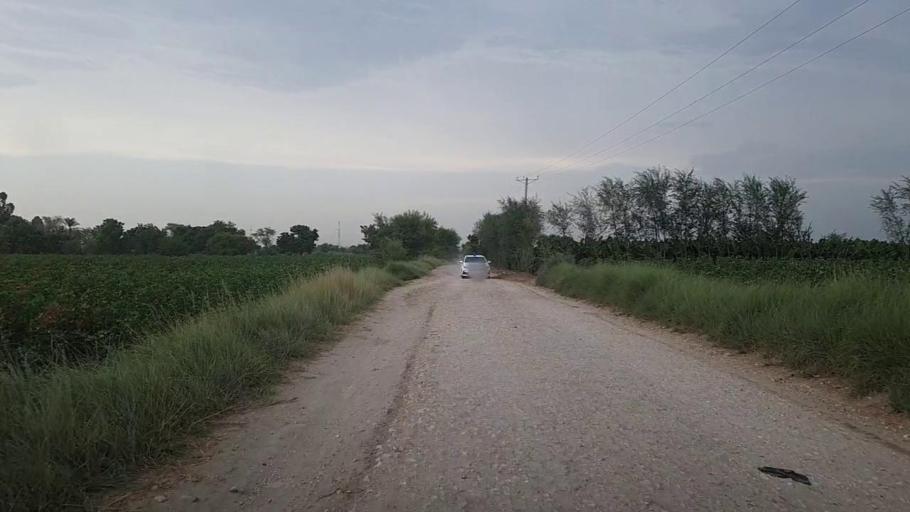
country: PK
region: Sindh
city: Karaundi
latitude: 26.9771
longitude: 68.3438
